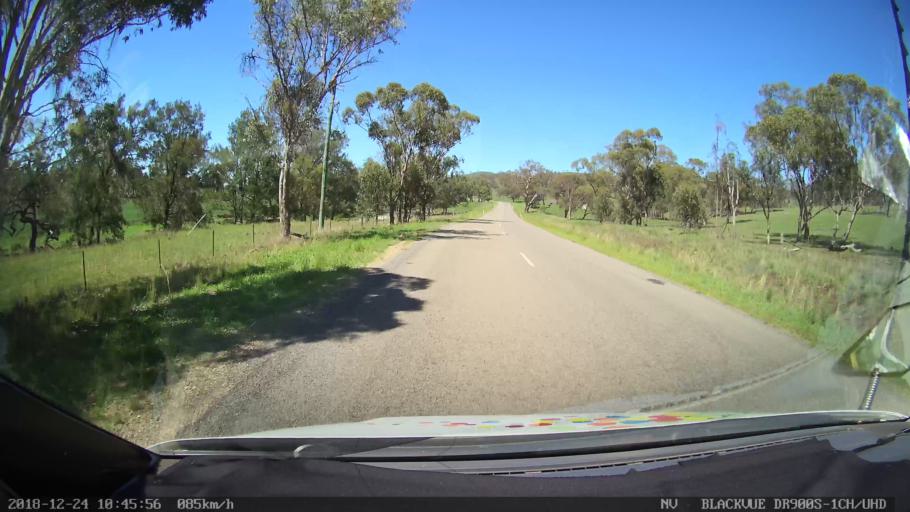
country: AU
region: New South Wales
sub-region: Upper Hunter Shire
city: Merriwa
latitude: -31.9075
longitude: 150.4321
